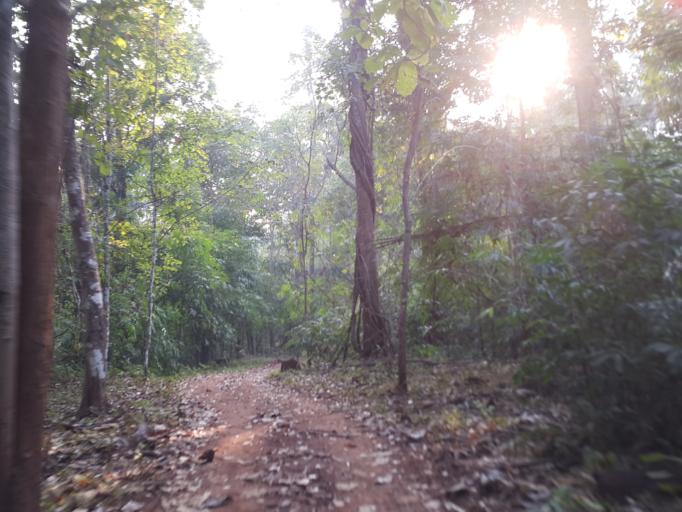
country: TH
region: Lamphun
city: Li
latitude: 17.6185
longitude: 98.9065
